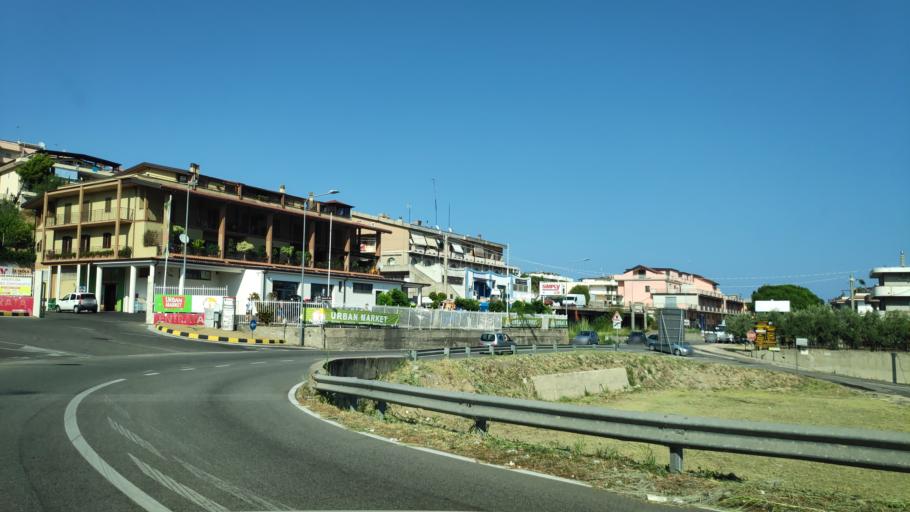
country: IT
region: Calabria
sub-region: Provincia di Catanzaro
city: Martelli-Laganosa
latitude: 38.6796
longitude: 16.5387
